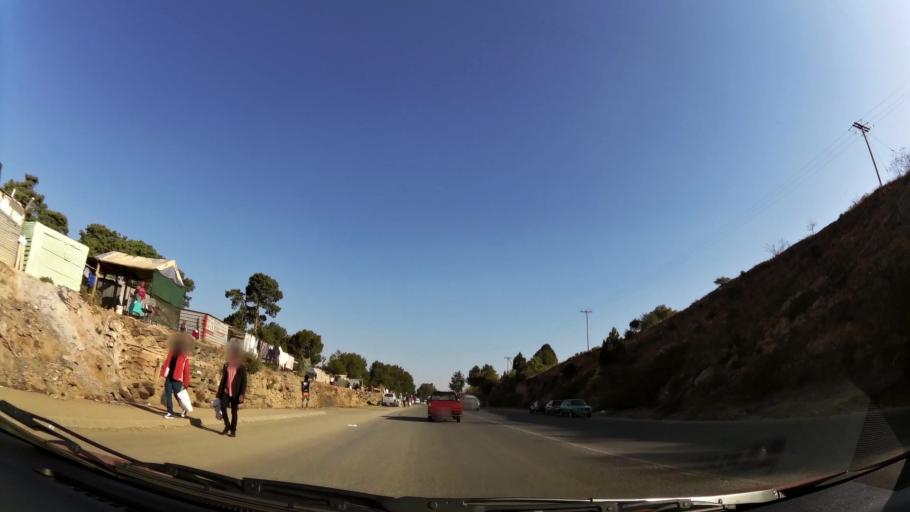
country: ZA
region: Gauteng
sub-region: West Rand District Municipality
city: Muldersdriseloop
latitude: -26.0536
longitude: 27.9047
